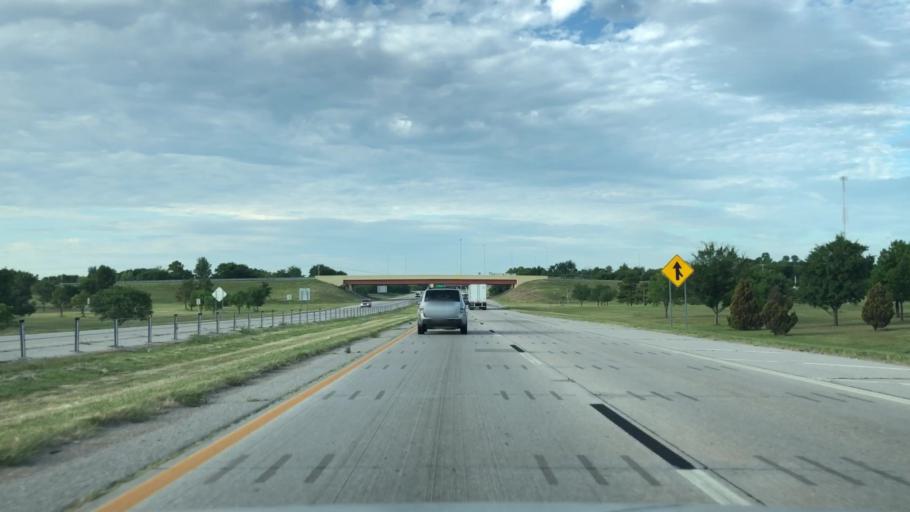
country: US
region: Oklahoma
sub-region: Tulsa County
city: Turley
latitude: 36.2089
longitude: -95.9462
